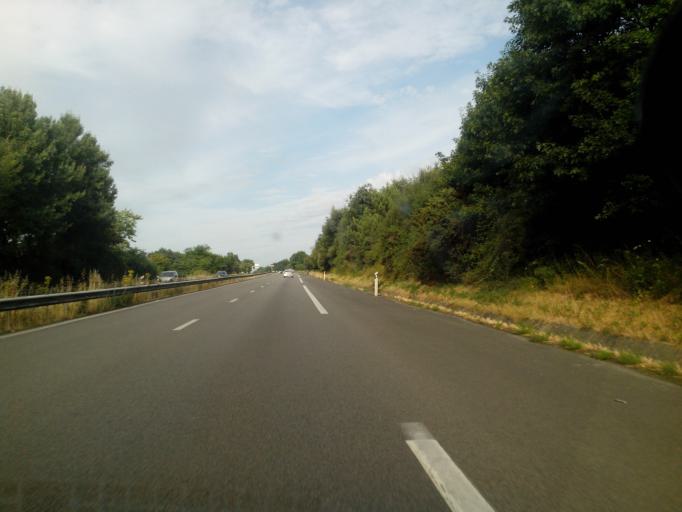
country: FR
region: Pays de la Loire
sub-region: Departement de la Loire-Atlantique
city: Orvault
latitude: 47.2573
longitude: -1.6365
